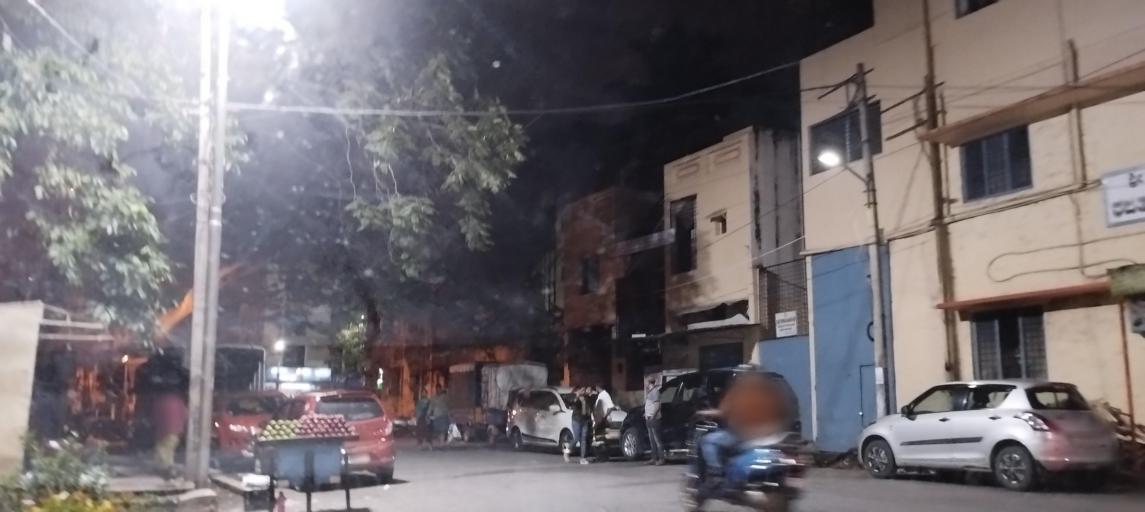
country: IN
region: Karnataka
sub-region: Bangalore Urban
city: Bangalore
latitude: 12.9375
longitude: 77.5703
